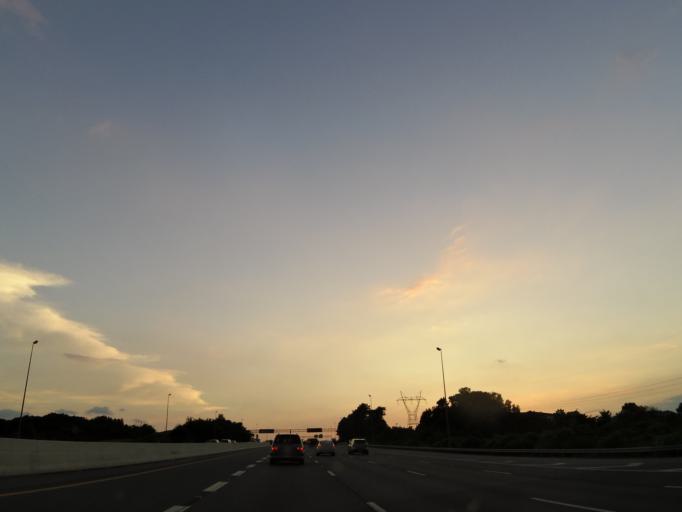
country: US
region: Tennessee
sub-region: Davidson County
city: Nashville
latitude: 36.1421
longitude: -86.6787
